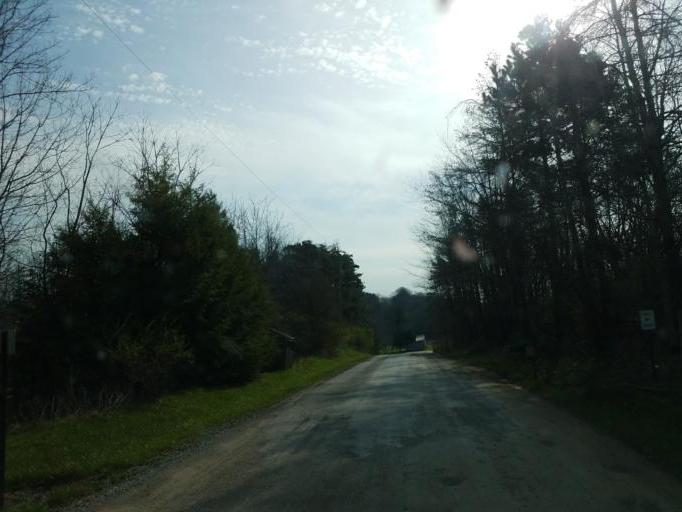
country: US
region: Ohio
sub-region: Richland County
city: Lexington
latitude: 40.5719
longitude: -82.6240
